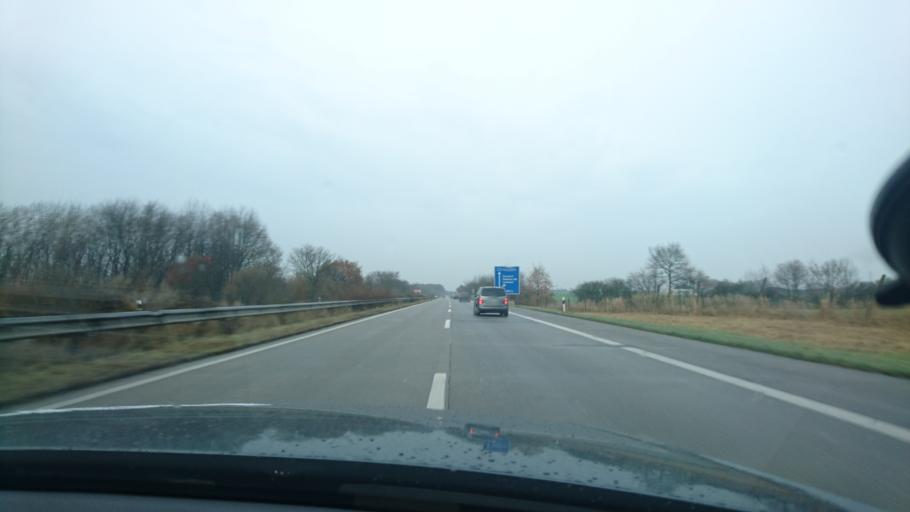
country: DE
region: Schleswig-Holstein
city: Scharbeutz
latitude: 53.9961
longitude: 10.7323
